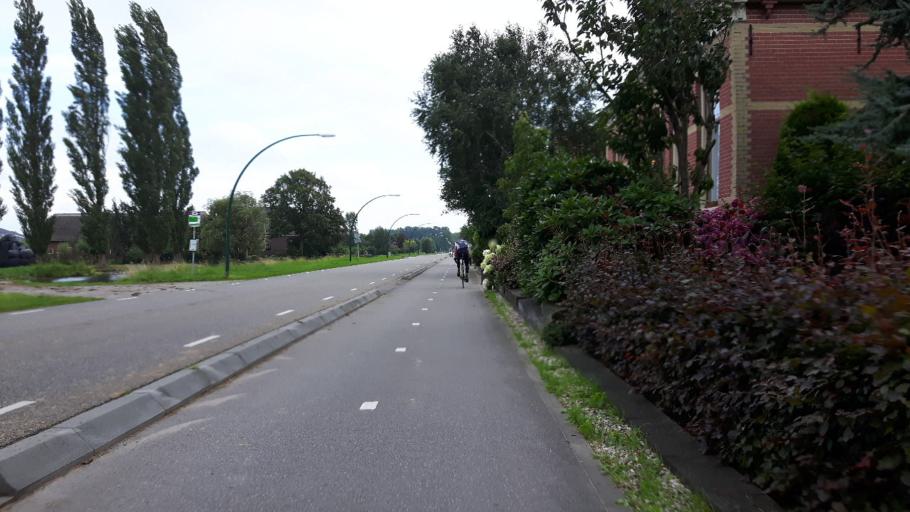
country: NL
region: Utrecht
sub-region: Gemeente Woerden
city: Woerden
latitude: 52.1019
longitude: 4.8549
